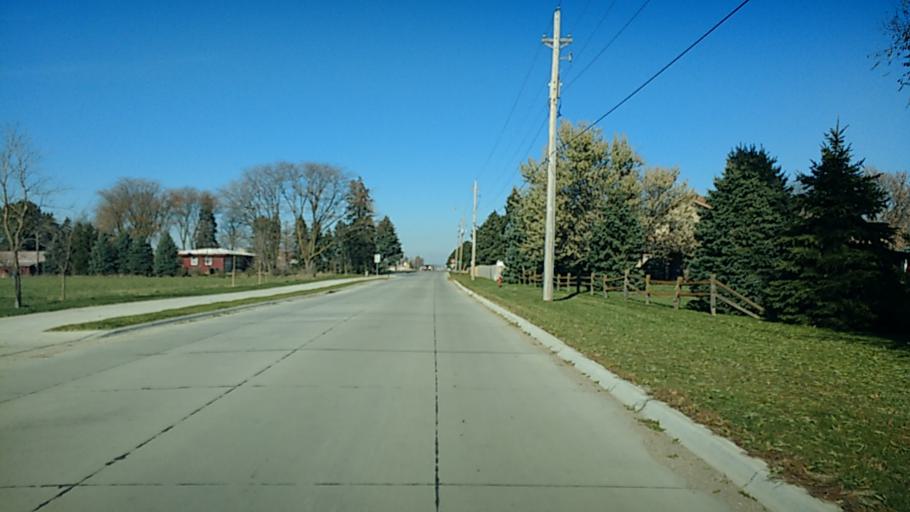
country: US
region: South Dakota
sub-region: Union County
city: North Sioux City
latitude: 42.5449
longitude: -96.5266
